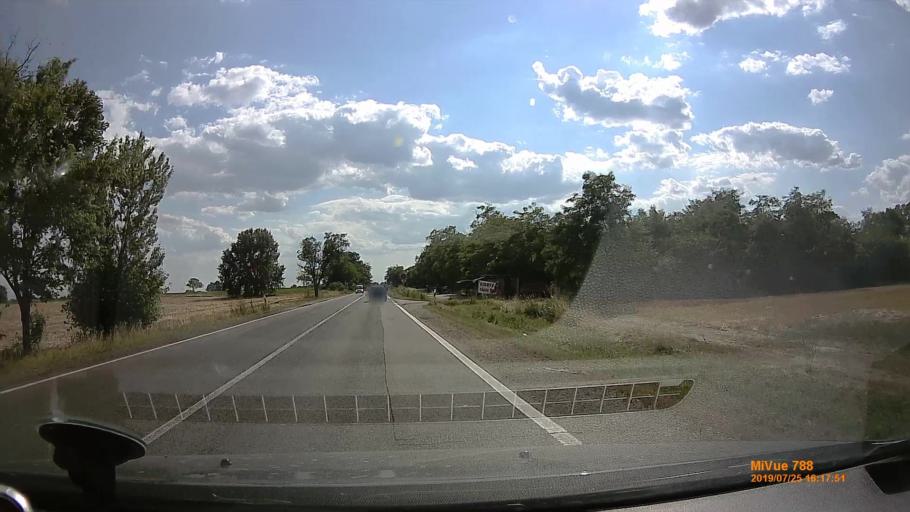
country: HU
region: Heves
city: Kal
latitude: 47.7655
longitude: 20.2685
